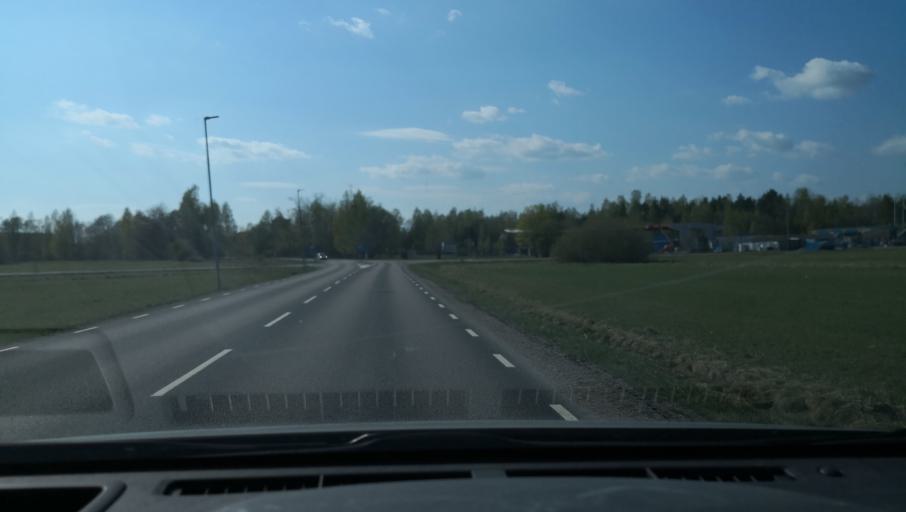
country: SE
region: Vaestmanland
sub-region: Sala Kommun
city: Sala
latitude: 59.9295
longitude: 16.6003
